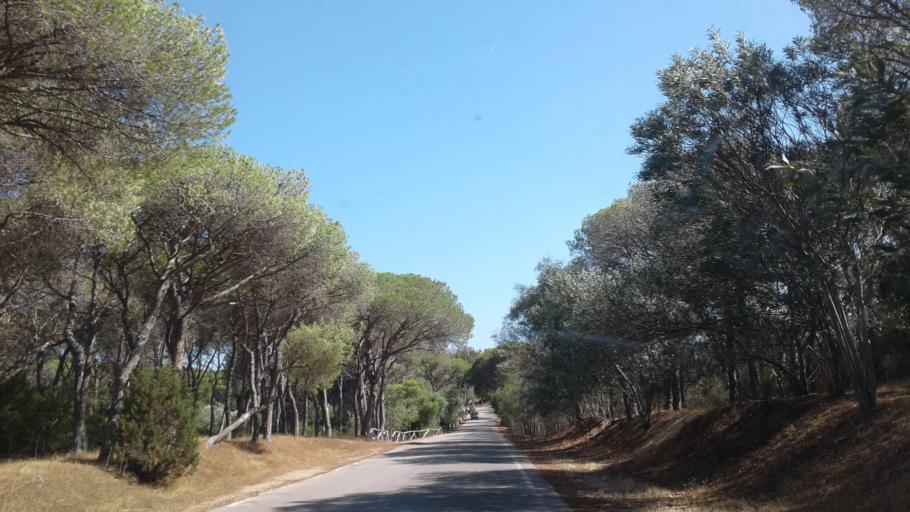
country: IT
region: Sardinia
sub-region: Provincia di Olbia-Tempio
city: La Maddalena
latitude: 41.2133
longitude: 9.4546
